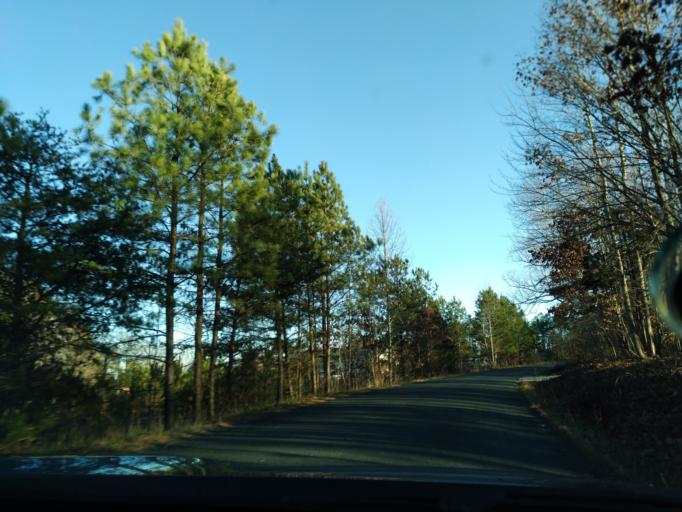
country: US
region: Virginia
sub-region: Buckingham County
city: Buckingham
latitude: 37.3698
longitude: -78.6178
